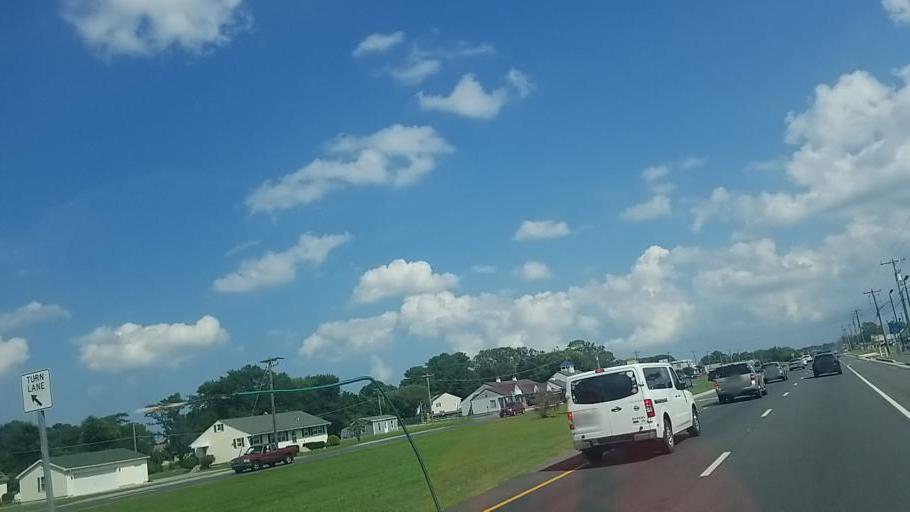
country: US
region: Delaware
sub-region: Sussex County
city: Millsboro
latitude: 38.5917
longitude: -75.3065
